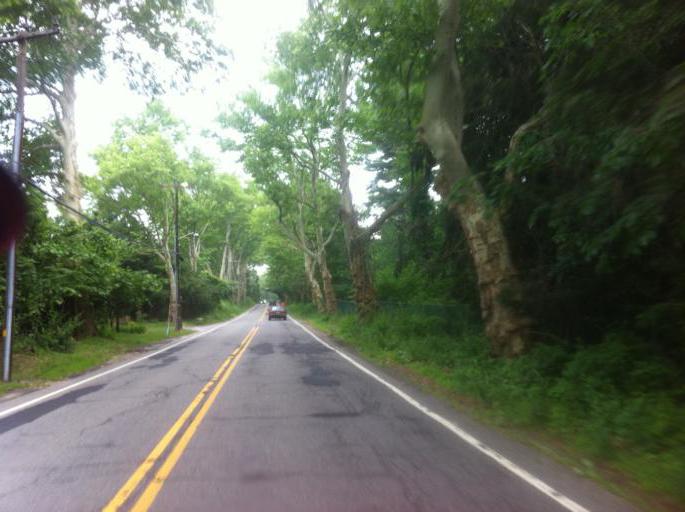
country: US
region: New York
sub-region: Nassau County
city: Upper Brookville
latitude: 40.8660
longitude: -73.5680
